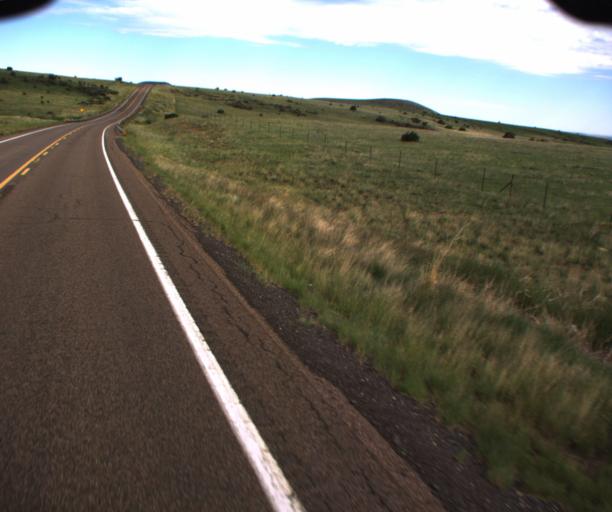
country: US
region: Arizona
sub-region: Apache County
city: Springerville
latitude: 34.2220
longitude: -109.4833
